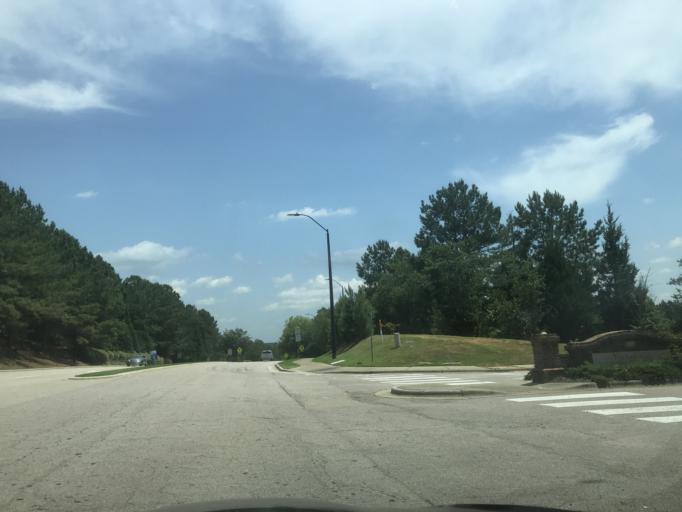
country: US
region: North Carolina
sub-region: Wake County
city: Wake Forest
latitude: 35.9495
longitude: -78.5697
